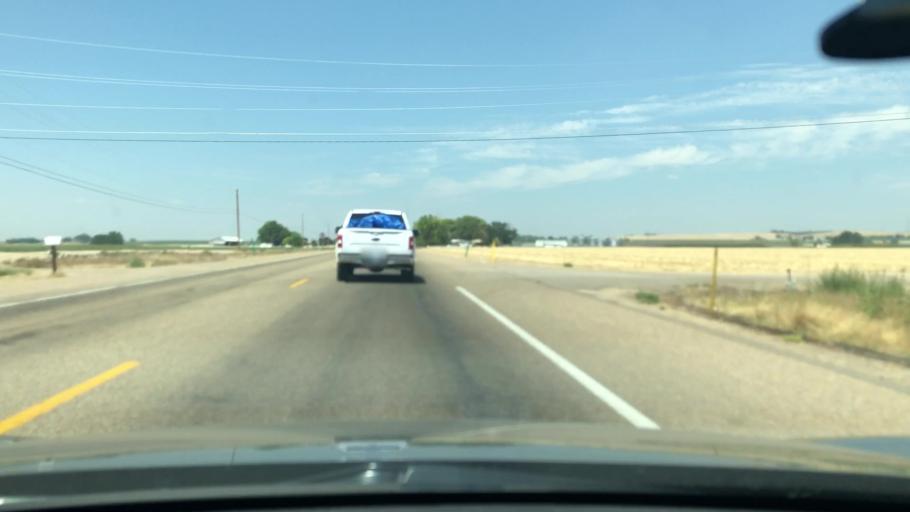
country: US
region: Idaho
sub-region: Canyon County
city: Parma
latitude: 43.7957
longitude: -116.9522
